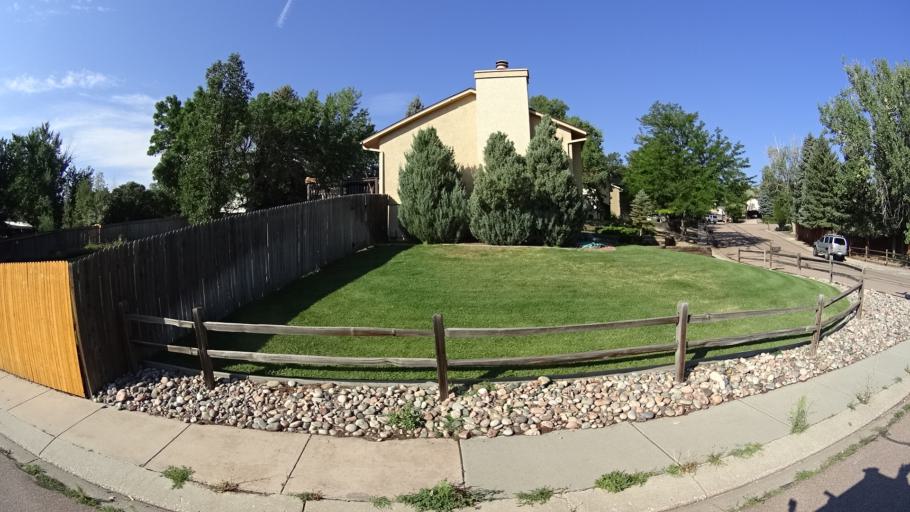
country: US
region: Colorado
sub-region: El Paso County
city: Colorado Springs
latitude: 38.8843
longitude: -104.8430
